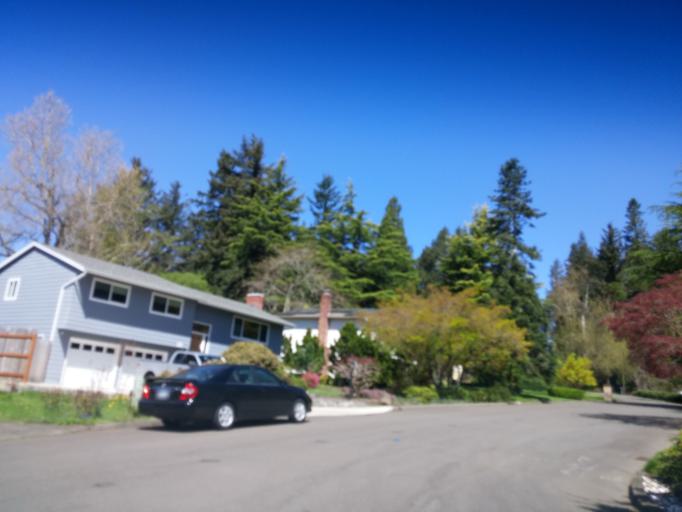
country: US
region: Oregon
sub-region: Washington County
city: West Haven
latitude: 45.5190
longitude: -122.7793
